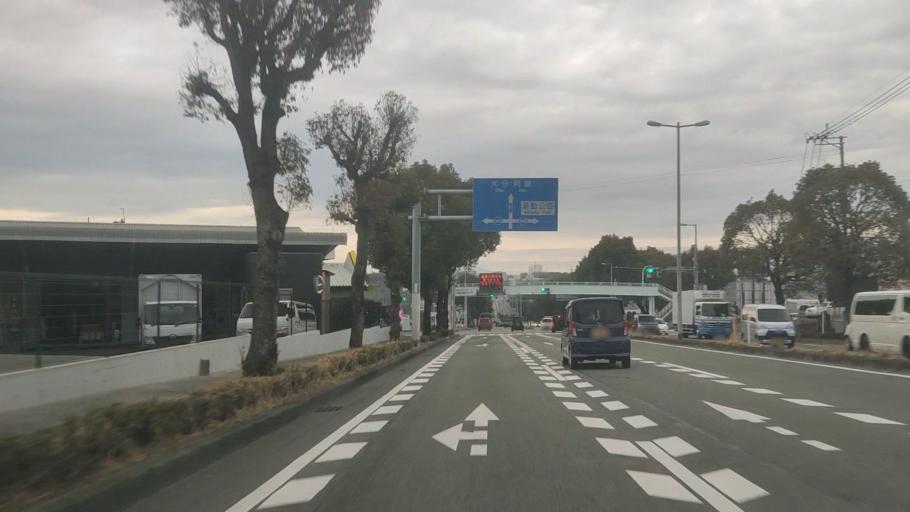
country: JP
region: Kumamoto
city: Ozu
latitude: 32.8420
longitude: 130.7805
